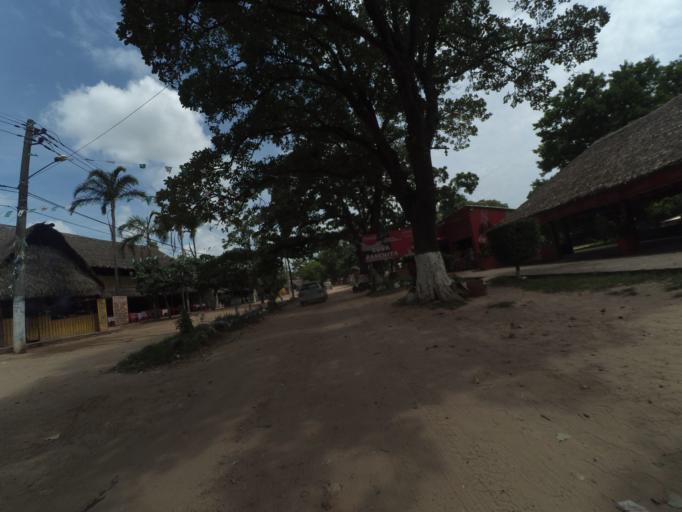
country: BO
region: Santa Cruz
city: Santa Cruz de la Sierra
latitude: -17.7841
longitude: -63.2247
